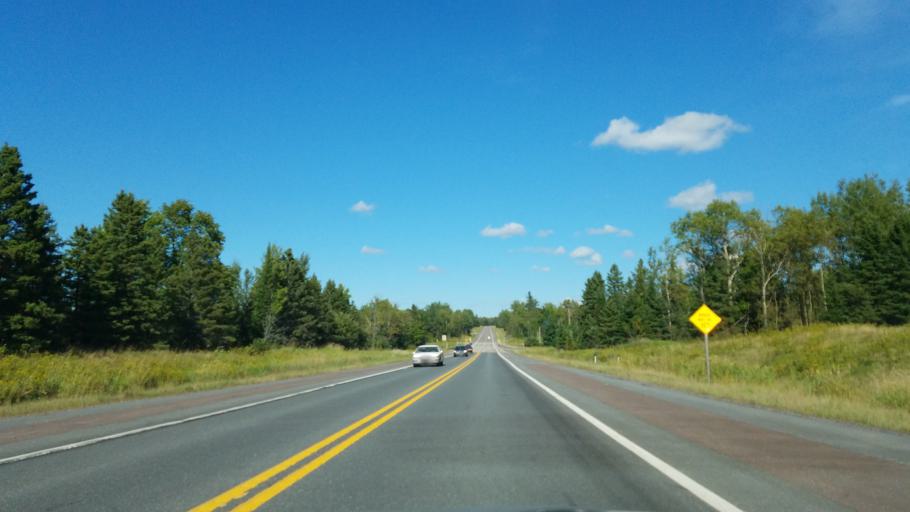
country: US
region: Michigan
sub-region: Baraga County
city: L'Anse
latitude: 46.5712
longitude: -88.4966
